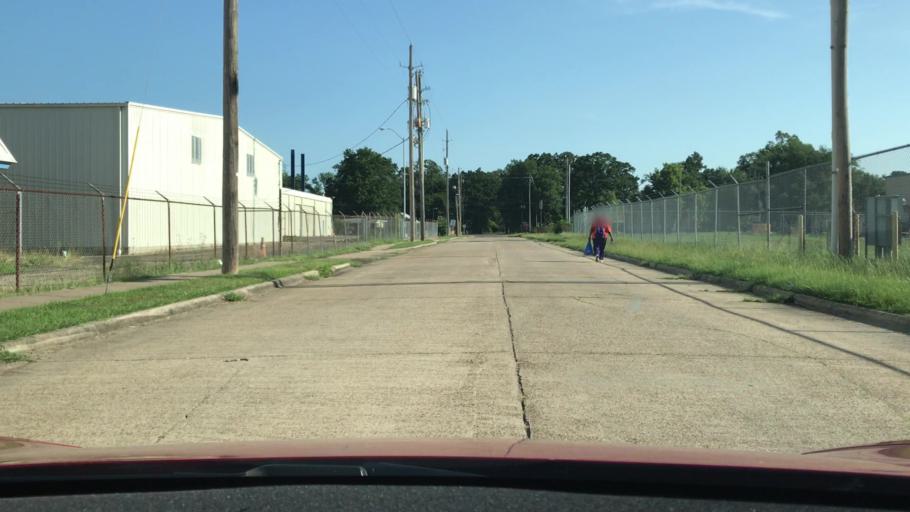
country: US
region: Louisiana
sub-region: Bossier Parish
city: Bossier City
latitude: 32.4405
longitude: -93.7652
